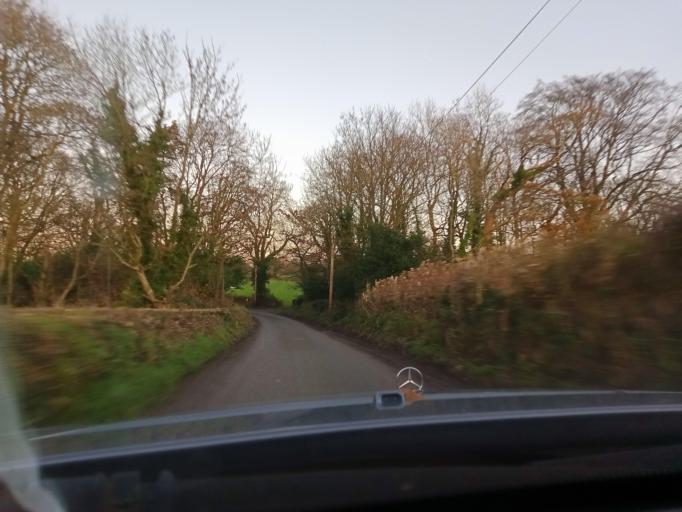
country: IE
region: Leinster
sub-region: Kilkenny
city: Thomastown
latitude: 52.4581
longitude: -7.1032
